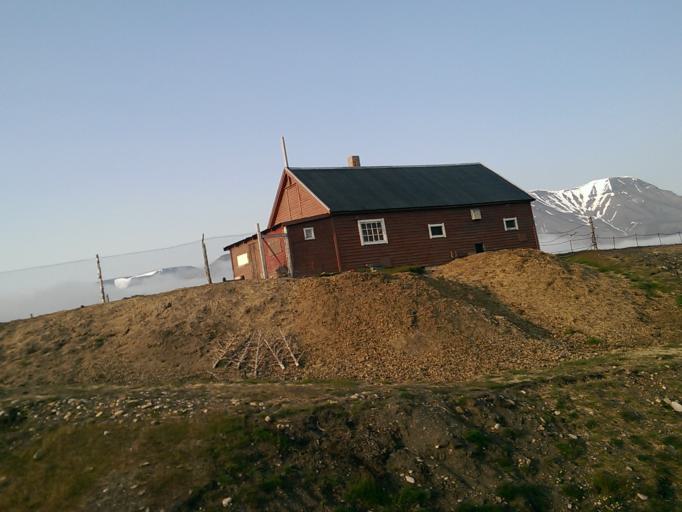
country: SJ
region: Svalbard
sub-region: Spitsbergen
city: Longyearbyen
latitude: 78.2422
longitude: 15.5275
